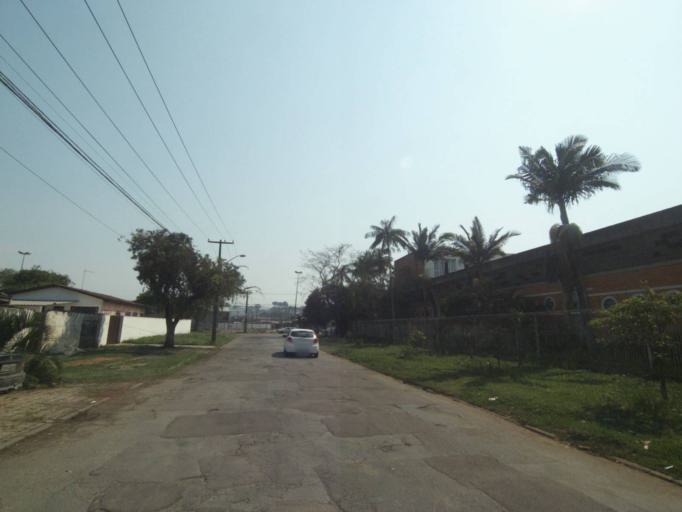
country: BR
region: Parana
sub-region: Curitiba
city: Curitiba
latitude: -25.4701
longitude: -49.2606
